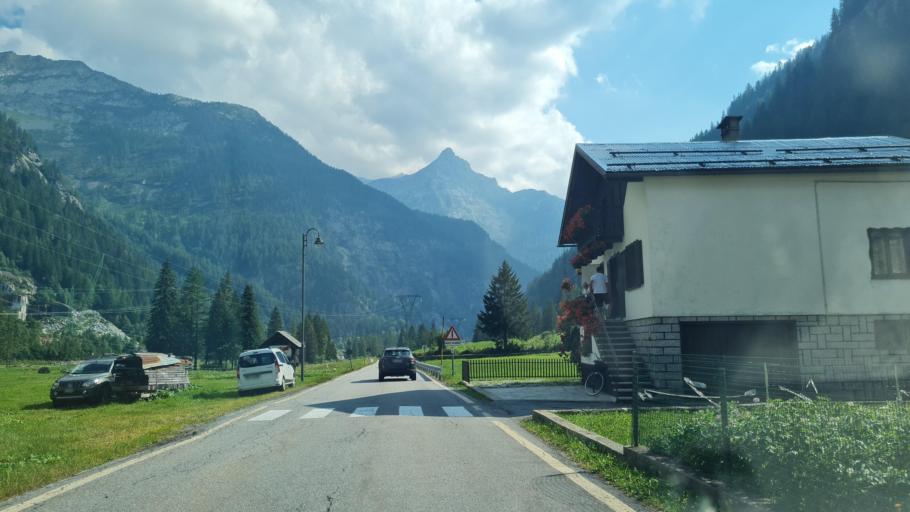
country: IT
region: Piedmont
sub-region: Provincia Verbano-Cusio-Ossola
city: Formazza
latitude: 46.3527
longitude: 8.4278
